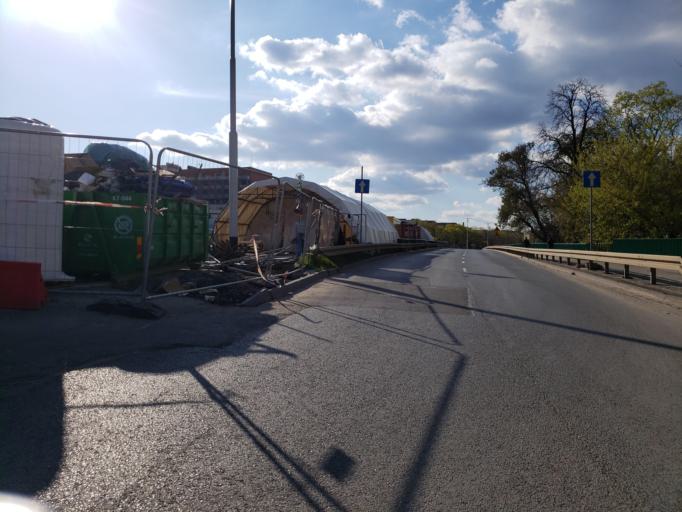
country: PL
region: Lower Silesian Voivodeship
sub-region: Powiat wroclawski
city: Wroclaw
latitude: 51.1172
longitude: 17.0194
